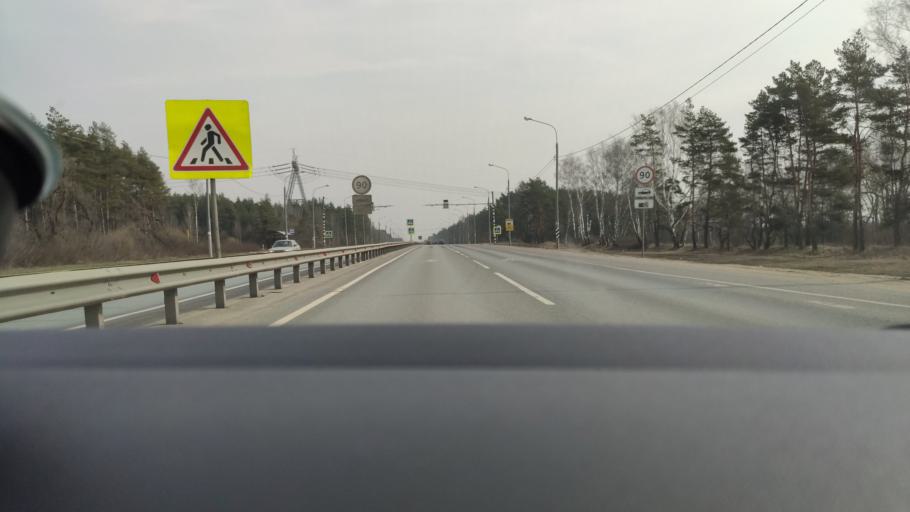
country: RU
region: Moskovskaya
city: Obukhovo
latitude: 55.8297
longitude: 38.2938
